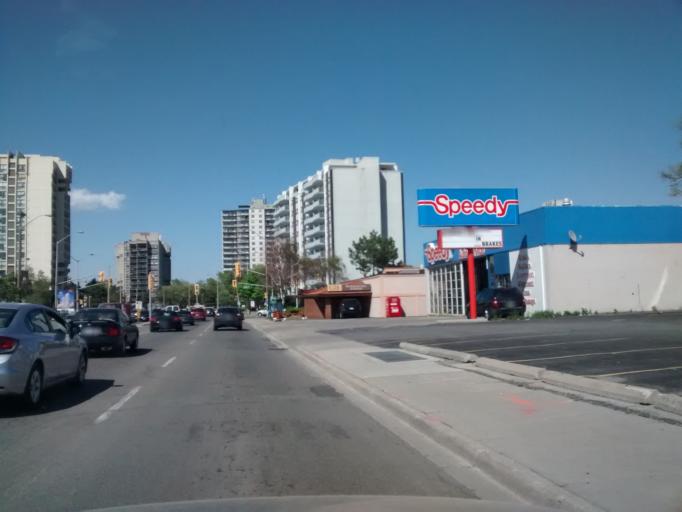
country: CA
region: Ontario
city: Oakville
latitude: 43.4460
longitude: -79.6876
